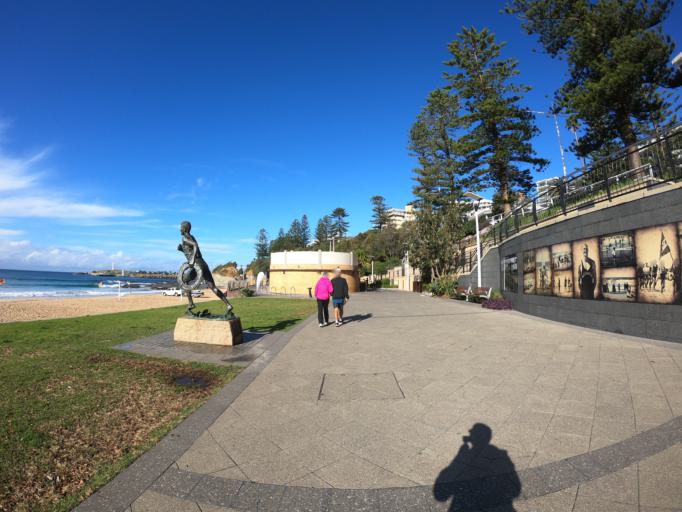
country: AU
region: New South Wales
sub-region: Wollongong
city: Wollongong
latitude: -34.4145
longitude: 150.9011
